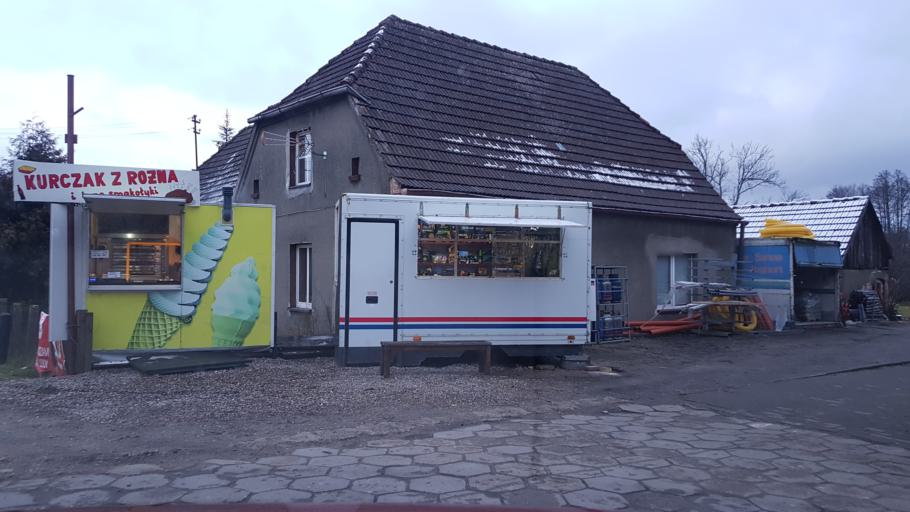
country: PL
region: Pomeranian Voivodeship
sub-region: Powiat bytowski
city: Tuchomie
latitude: 54.1128
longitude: 17.3354
